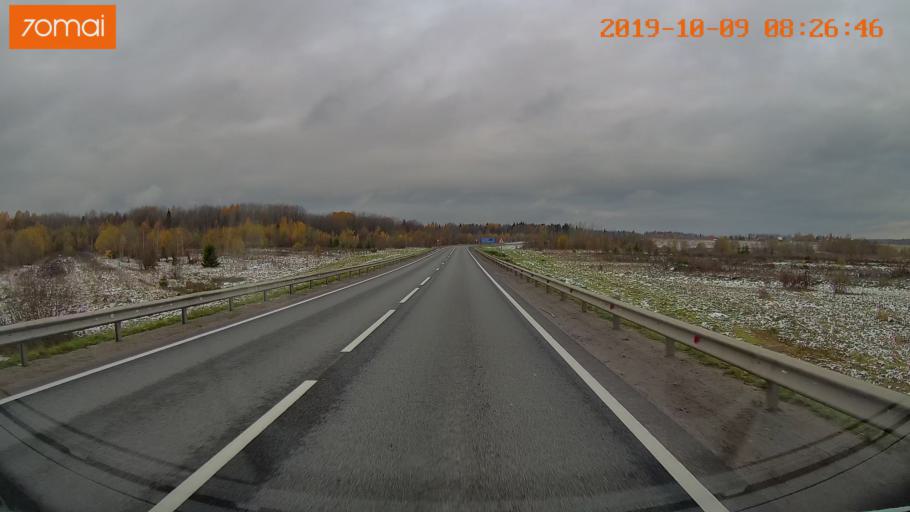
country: RU
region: Vologda
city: Gryazovets
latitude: 58.7965
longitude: 40.2608
